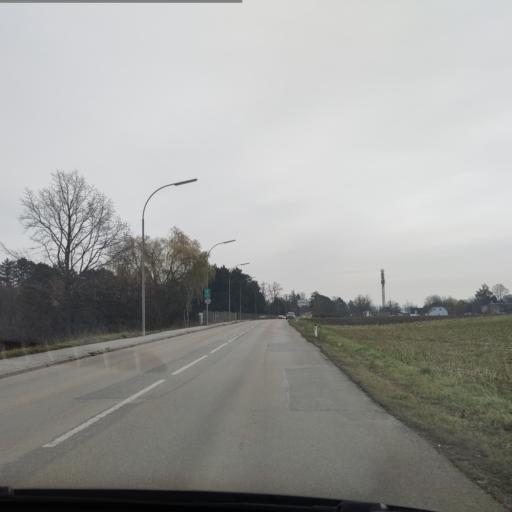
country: AT
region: Lower Austria
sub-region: Sankt Polten Stadt
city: Sankt Poelten
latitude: 48.2164
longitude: 15.6073
